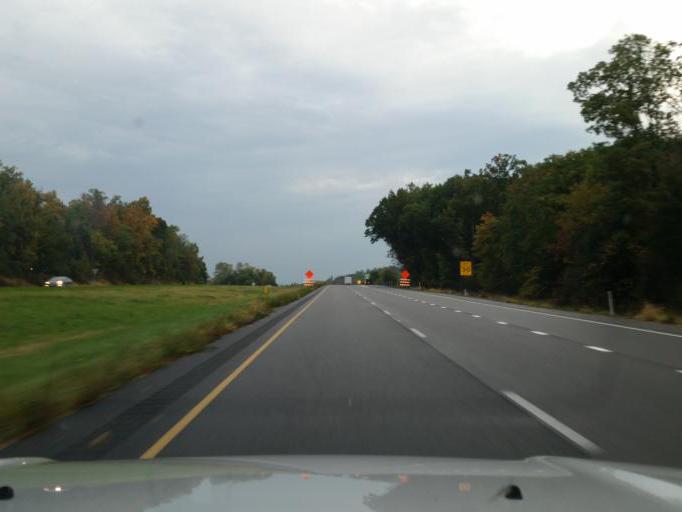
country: US
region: Pennsylvania
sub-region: Adams County
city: Lake Heritage
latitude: 39.8293
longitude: -77.1972
